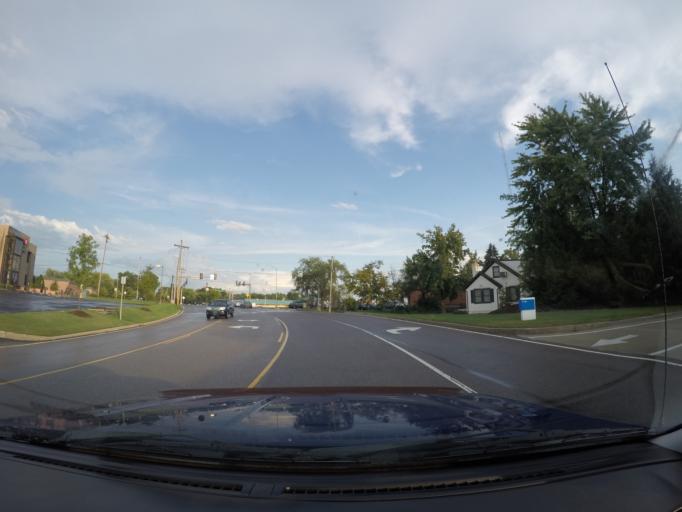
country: US
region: Missouri
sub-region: Saint Louis County
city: Sunset Hills
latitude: 38.5512
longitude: -90.4080
